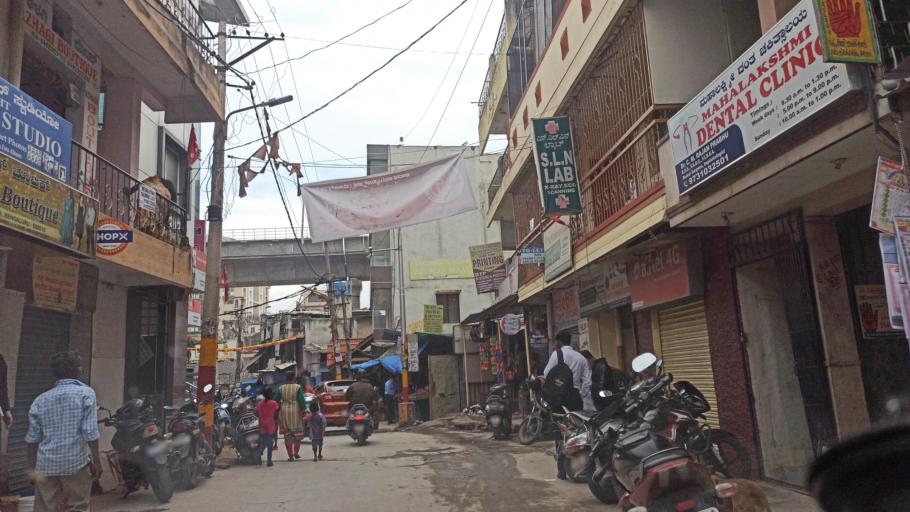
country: IN
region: Karnataka
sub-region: Bangalore Urban
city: Bangalore
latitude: 12.9969
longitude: 77.6719
